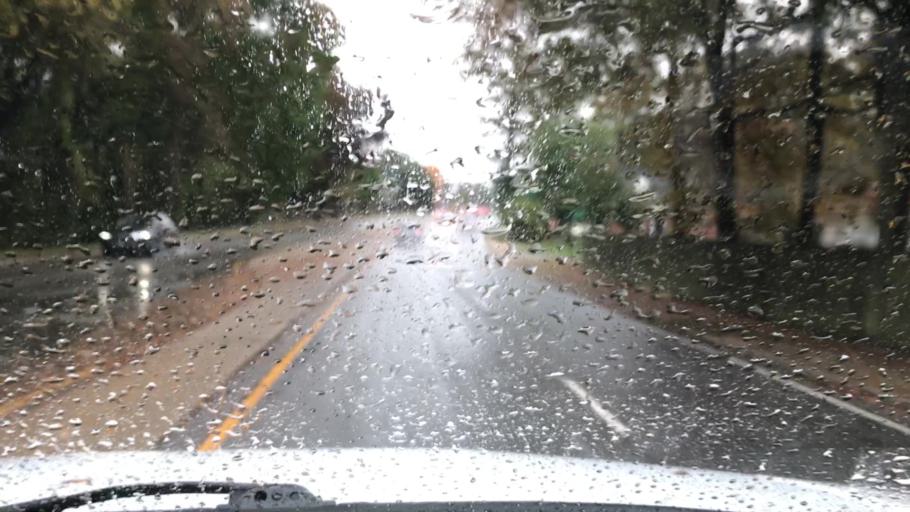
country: US
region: Virginia
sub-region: Henrico County
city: Tuckahoe
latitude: 37.5930
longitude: -77.5373
